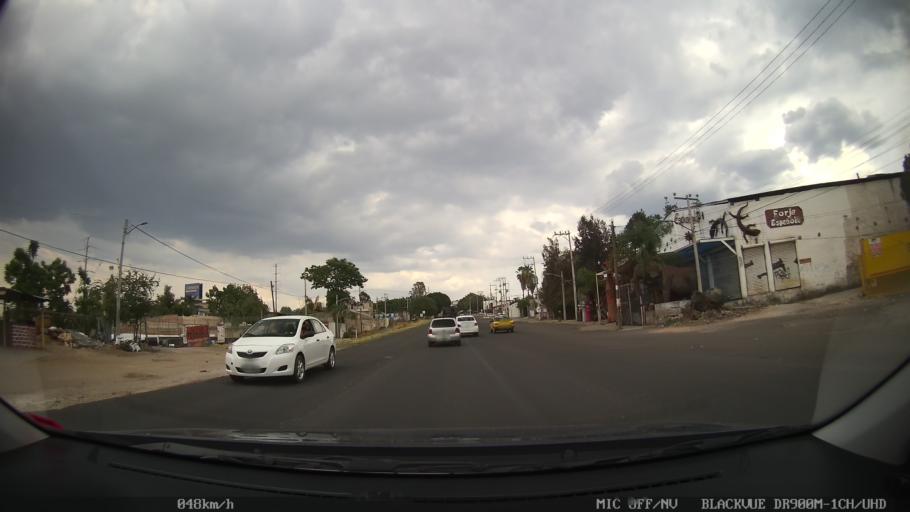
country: MX
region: Jalisco
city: Tlaquepaque
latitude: 20.6172
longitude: -103.2707
